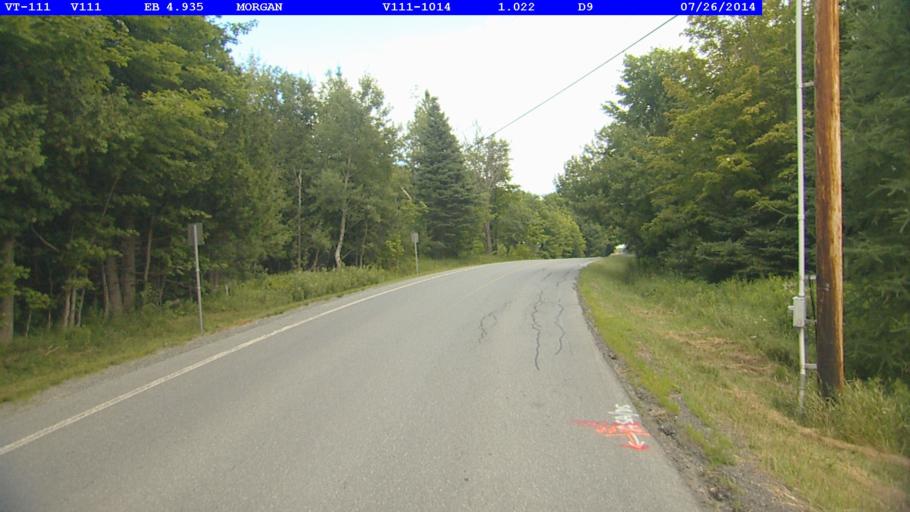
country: US
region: Vermont
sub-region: Orleans County
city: Newport
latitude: 44.9248
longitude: -72.0465
